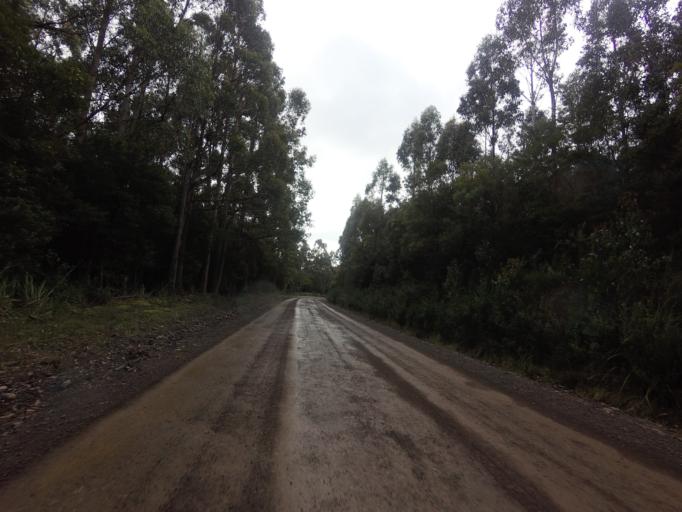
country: AU
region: Tasmania
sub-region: Huon Valley
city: Geeveston
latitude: -43.4687
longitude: 146.8934
